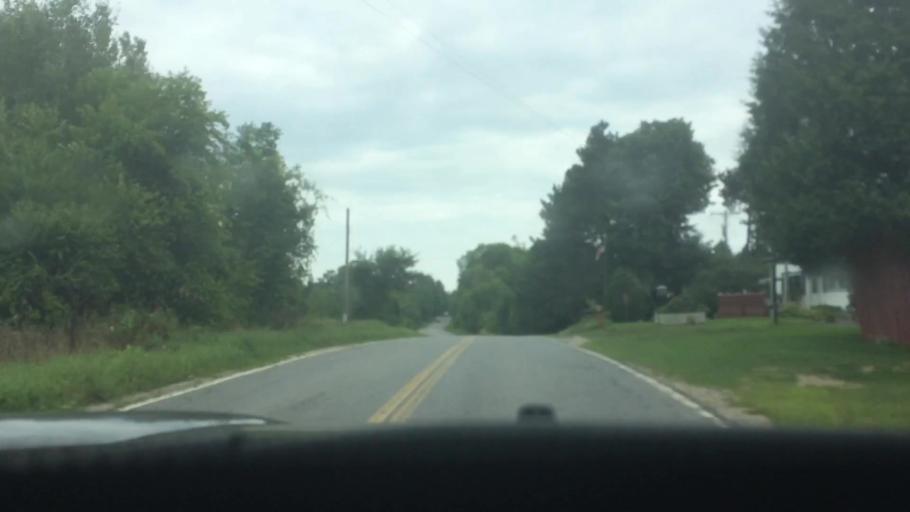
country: US
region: New York
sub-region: St. Lawrence County
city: Hannawa Falls
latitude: 44.5747
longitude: -74.9036
